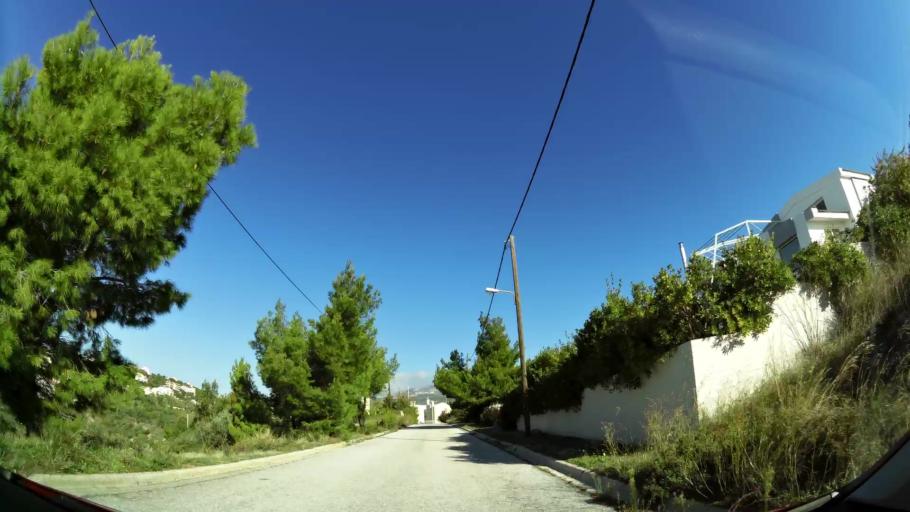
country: GR
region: Attica
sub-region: Nomarchia Anatolikis Attikis
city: Dhrafi
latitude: 38.0258
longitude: 23.8995
